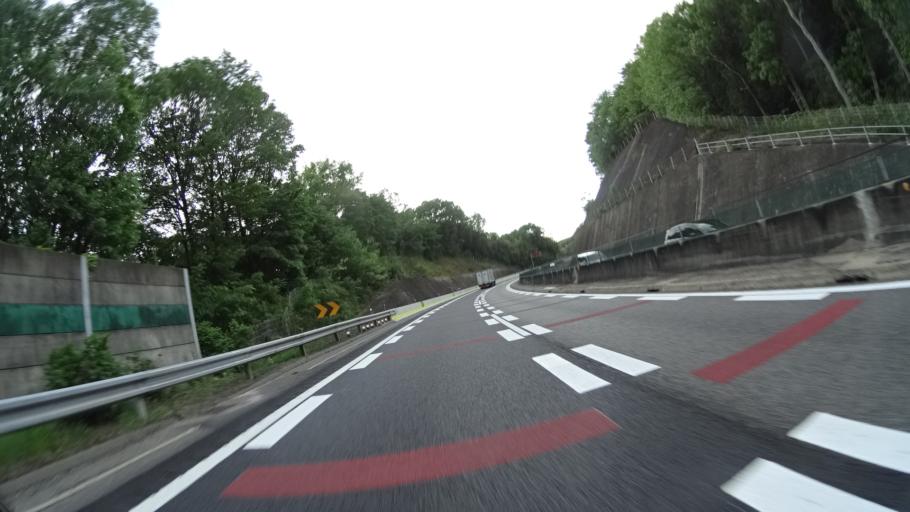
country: JP
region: Gifu
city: Toki
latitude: 35.3698
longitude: 137.2036
